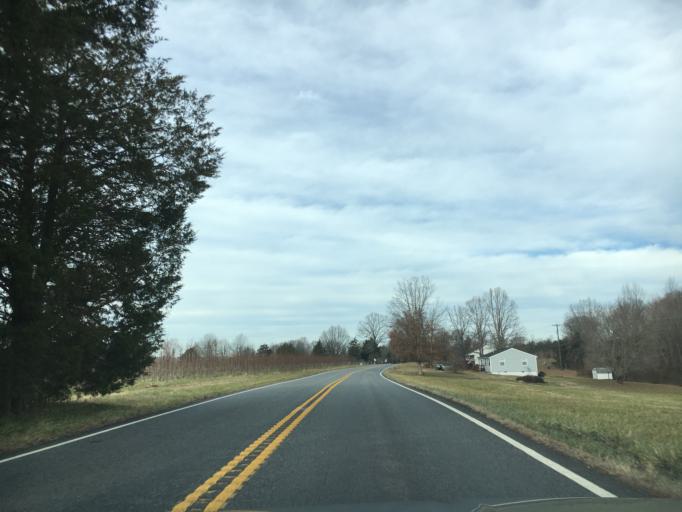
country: US
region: Virginia
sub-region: Goochland County
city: Goochland
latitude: 37.8242
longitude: -77.8901
